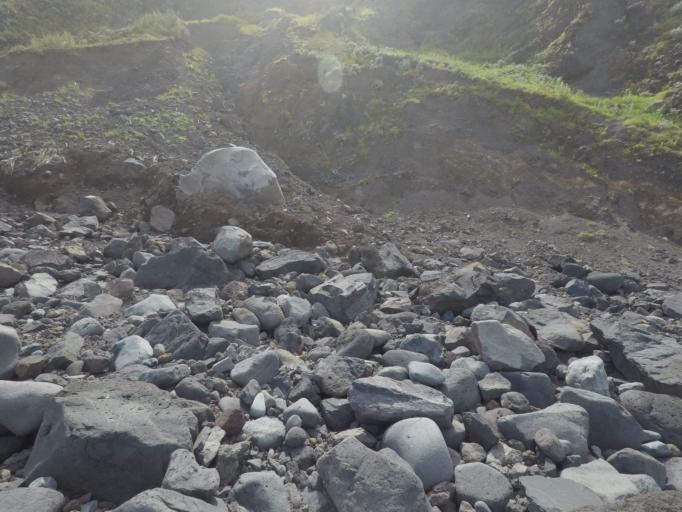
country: PT
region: Madeira
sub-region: Sao Vicente
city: Sao Vicente
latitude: 32.8267
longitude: -16.9950
